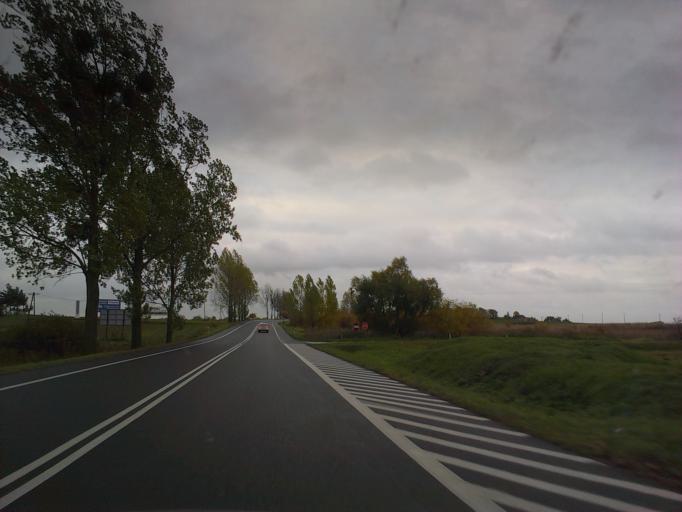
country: PL
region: Kujawsko-Pomorskie
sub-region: Powiat chelminski
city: Chelmno
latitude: 53.3153
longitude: 18.5068
